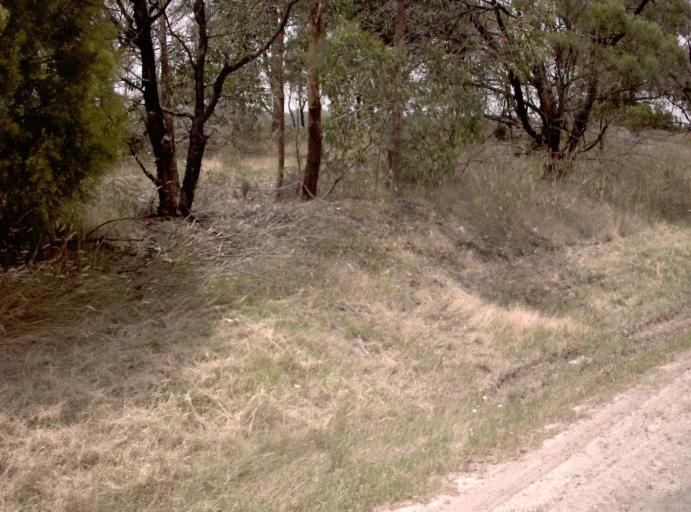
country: AU
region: Victoria
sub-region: Latrobe
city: Traralgon
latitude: -38.4480
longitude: 146.7356
